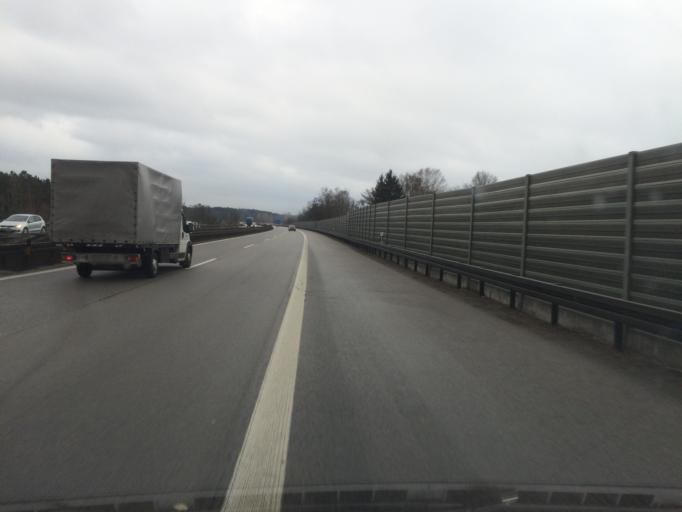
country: DE
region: Bavaria
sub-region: Upper Palatinate
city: Schwandorf in Bayern
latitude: 49.2711
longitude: 12.1261
